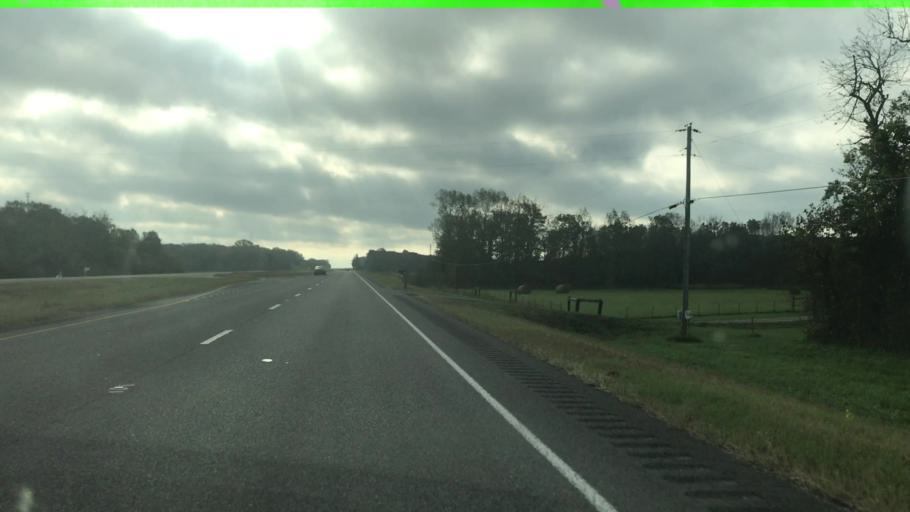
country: US
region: Alabama
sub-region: Morgan County
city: Danville
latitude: 34.4081
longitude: -87.1461
